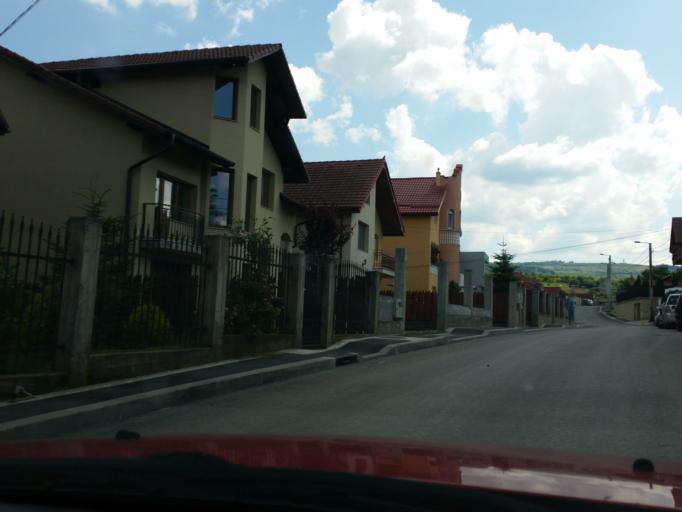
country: RO
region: Cluj
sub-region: Municipiul Cluj-Napoca
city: Cluj-Napoca
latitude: 46.7545
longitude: 23.6209
